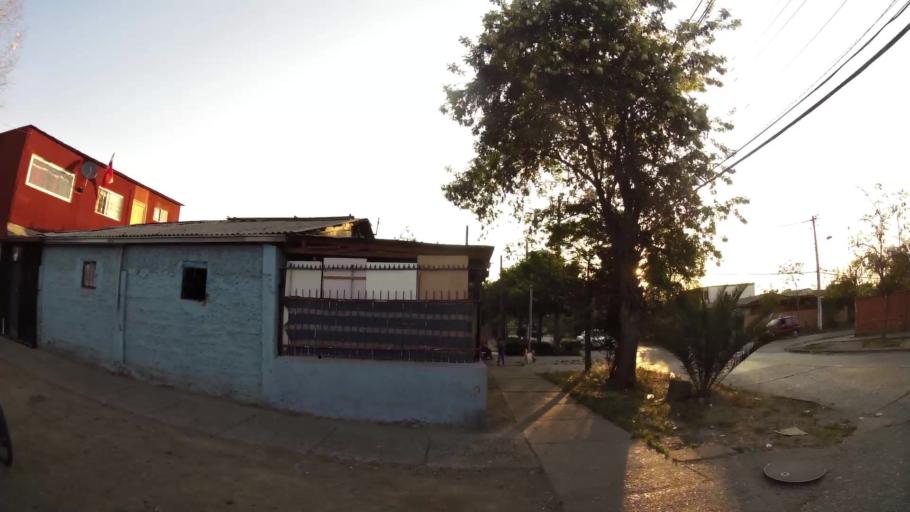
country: CL
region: Santiago Metropolitan
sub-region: Provincia de Santiago
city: Santiago
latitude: -33.5099
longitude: -70.6280
